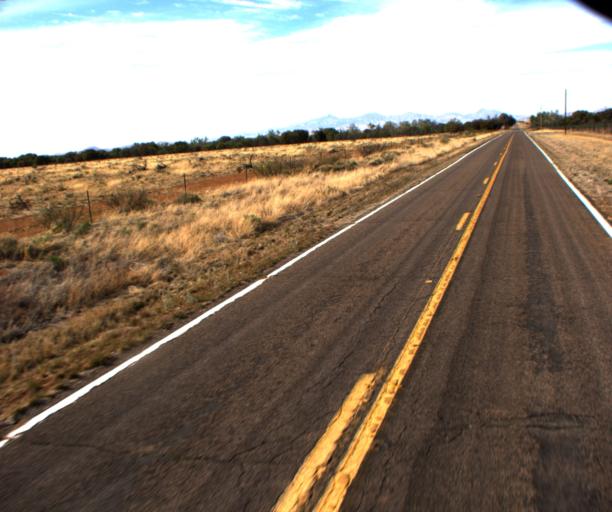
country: US
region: Arizona
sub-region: Cochise County
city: Willcox
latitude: 31.8833
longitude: -109.4913
